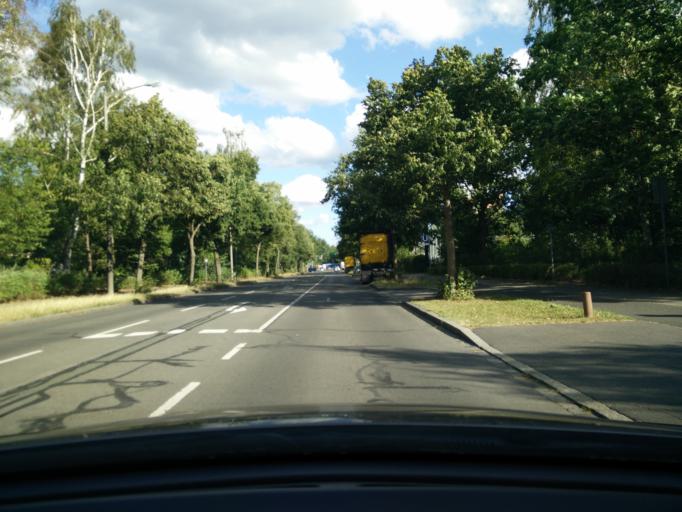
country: DE
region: Bavaria
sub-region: Regierungsbezirk Mittelfranken
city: Wendelstein
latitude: 49.3997
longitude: 11.1400
